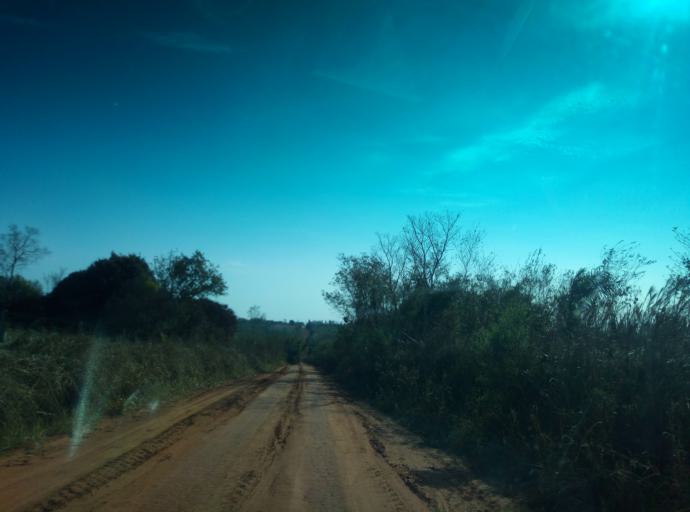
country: PY
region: Caaguazu
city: Doctor Cecilio Baez
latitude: -25.1648
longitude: -56.2201
